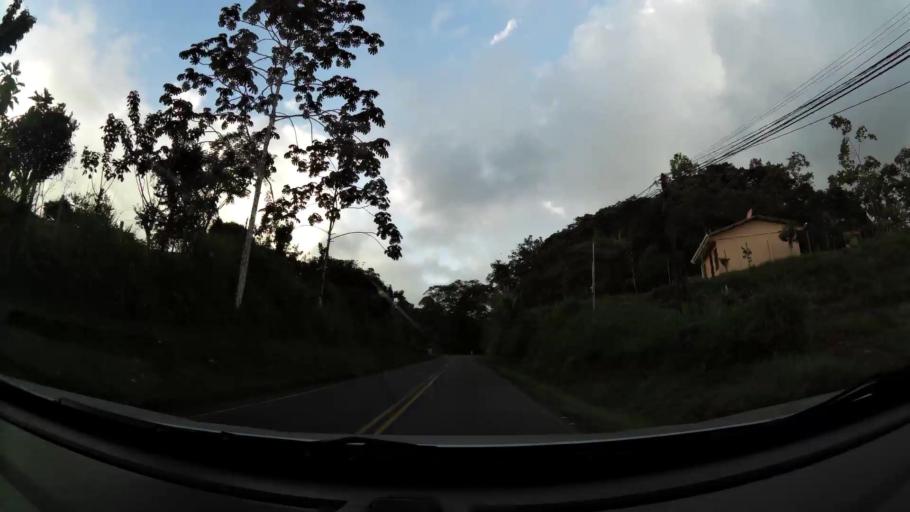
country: CR
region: Cartago
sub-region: Canton de Turrialba
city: La Suiza
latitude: 9.9753
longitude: -83.5698
